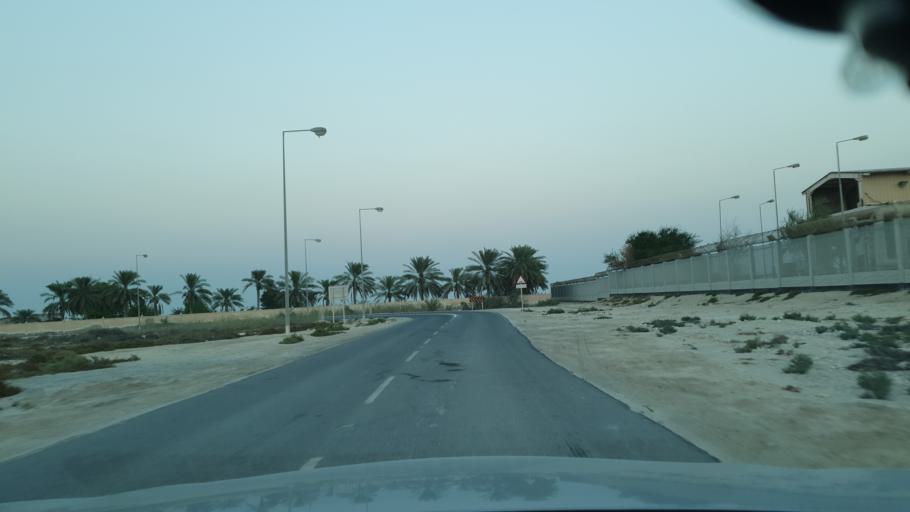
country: BH
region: Central Governorate
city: Dar Kulayb
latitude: 25.9766
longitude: 50.6136
